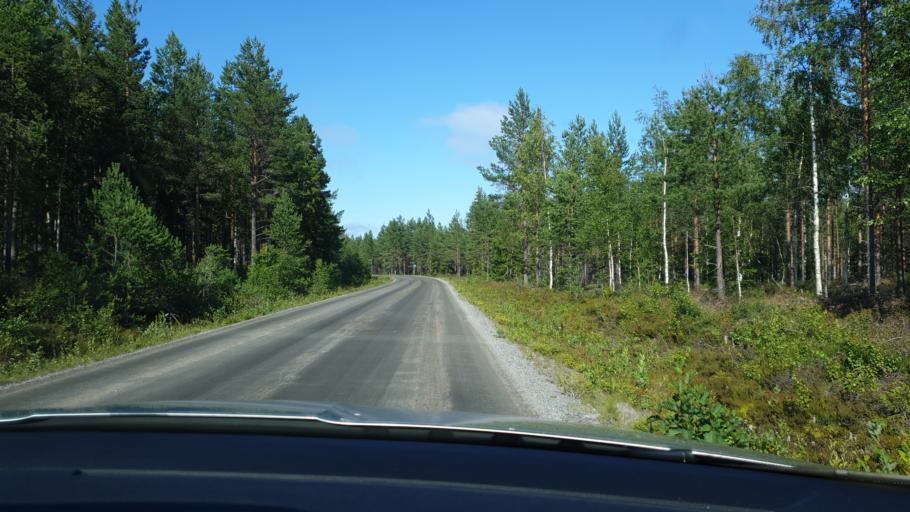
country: SE
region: Gaevleborg
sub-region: Soderhamns Kommun
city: Soderhamn
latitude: 61.4336
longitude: 17.0052
